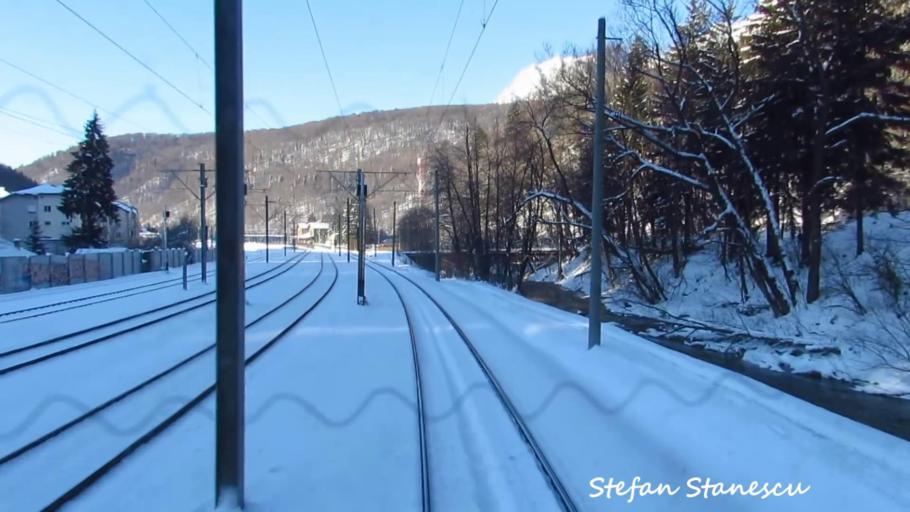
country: RO
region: Prahova
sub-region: Oras Azuga
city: Azuga
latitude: 45.4481
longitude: 25.5555
